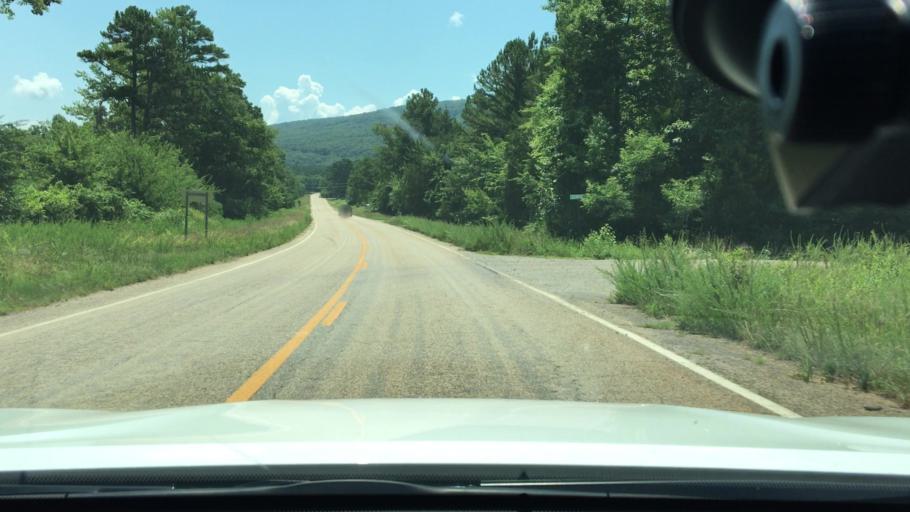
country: US
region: Arkansas
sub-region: Logan County
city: Paris
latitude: 35.1939
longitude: -93.6305
